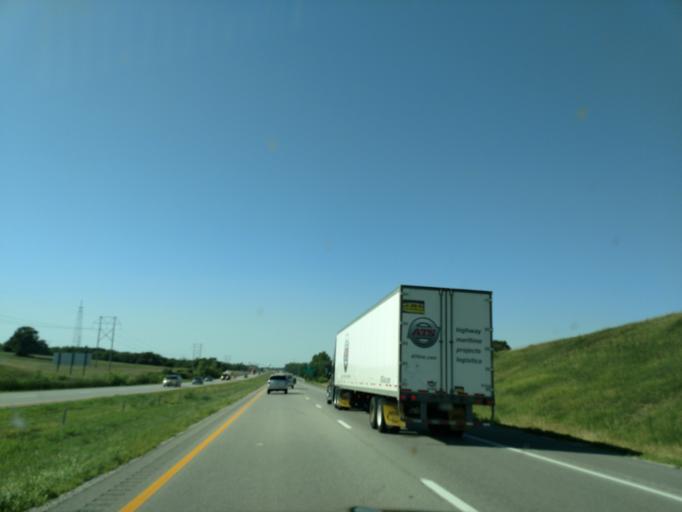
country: US
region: Missouri
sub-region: Buchanan County
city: Saint Joseph
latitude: 39.7574
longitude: -94.7907
